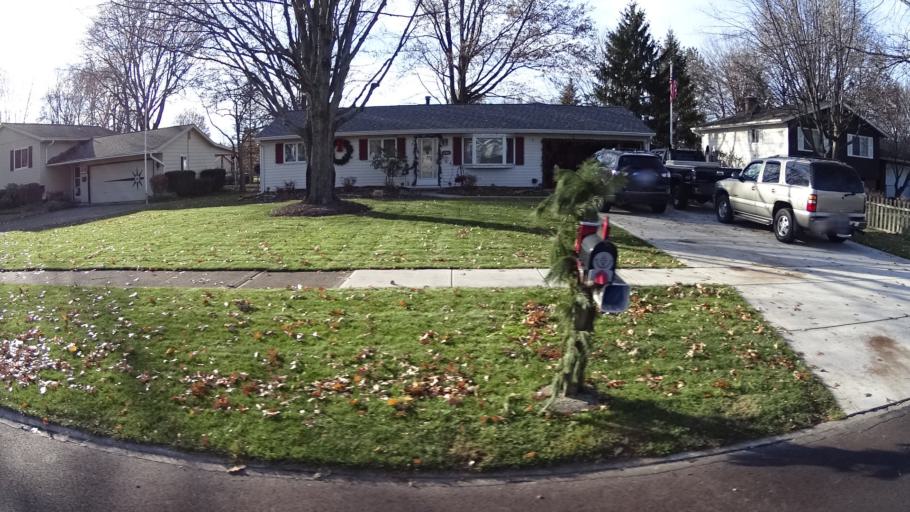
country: US
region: Ohio
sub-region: Lorain County
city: North Ridgeville
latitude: 41.3883
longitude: -81.9976
